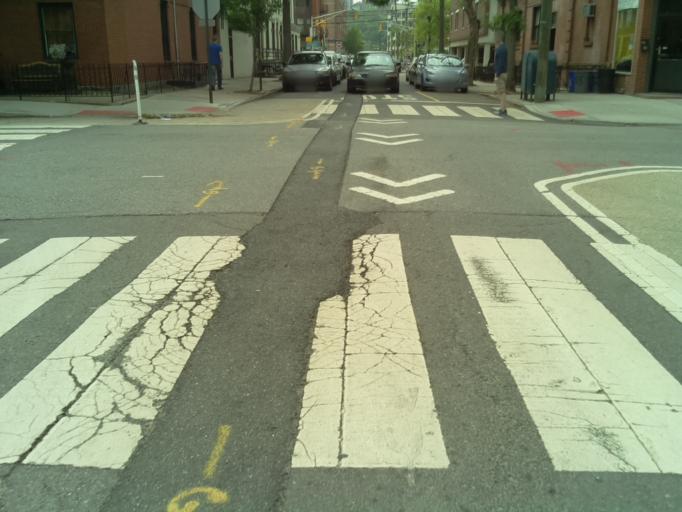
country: US
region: New Jersey
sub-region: Hudson County
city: Hoboken
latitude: 40.7516
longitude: -74.0294
